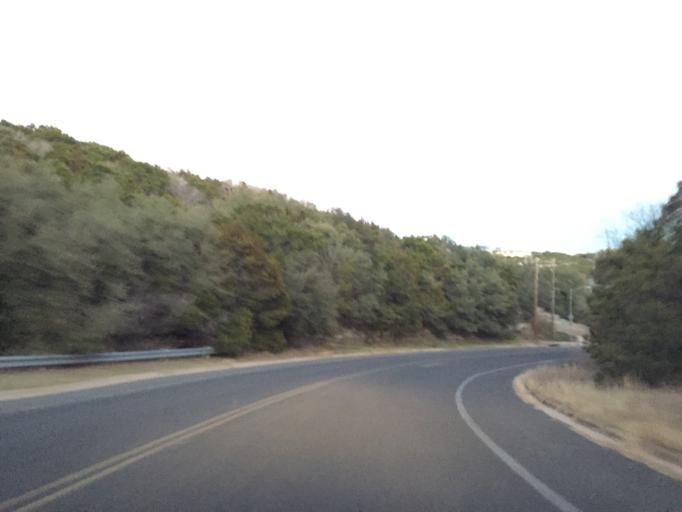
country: US
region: Texas
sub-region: Williamson County
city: Jollyville
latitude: 30.4016
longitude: -97.7634
